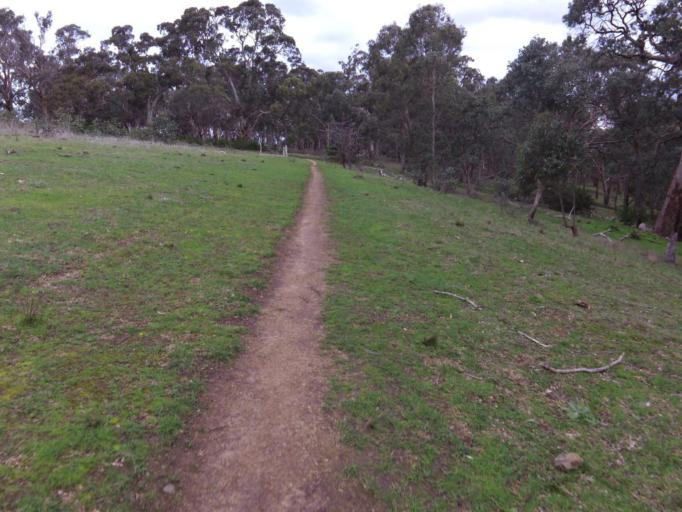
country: AU
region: Victoria
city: Plenty
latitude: -37.6723
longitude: 145.1001
